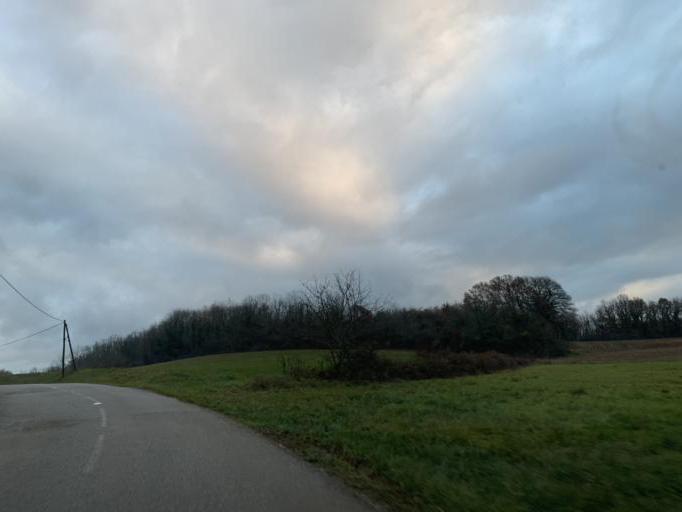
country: FR
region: Rhone-Alpes
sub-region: Departement de l'Ain
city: Belley
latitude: 45.7903
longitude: 5.6924
